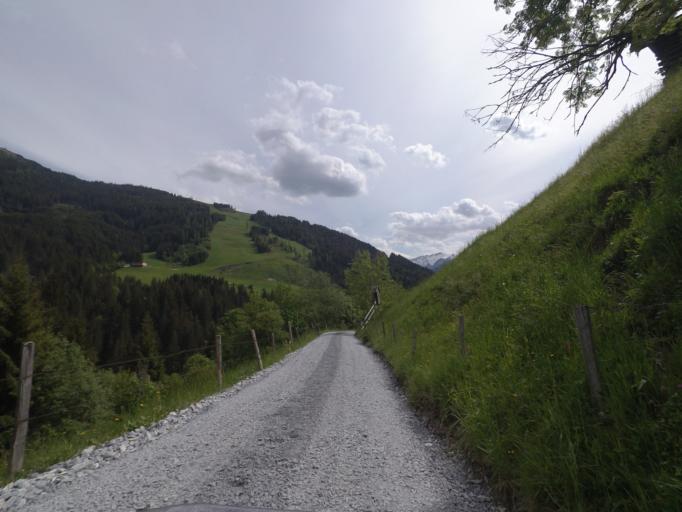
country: AT
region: Salzburg
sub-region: Politischer Bezirk Sankt Johann im Pongau
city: Dorfgastein
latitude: 47.2533
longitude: 13.1258
